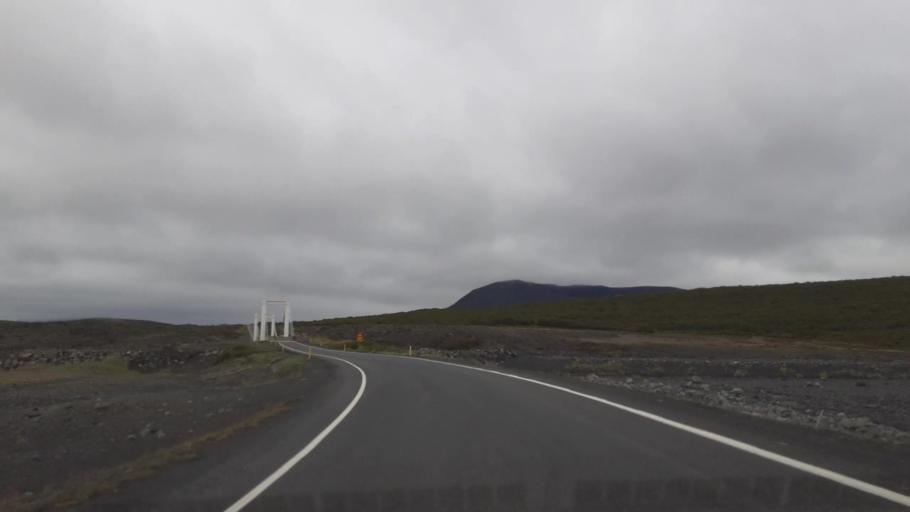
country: IS
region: Northeast
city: Husavik
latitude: 66.0313
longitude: -16.4470
